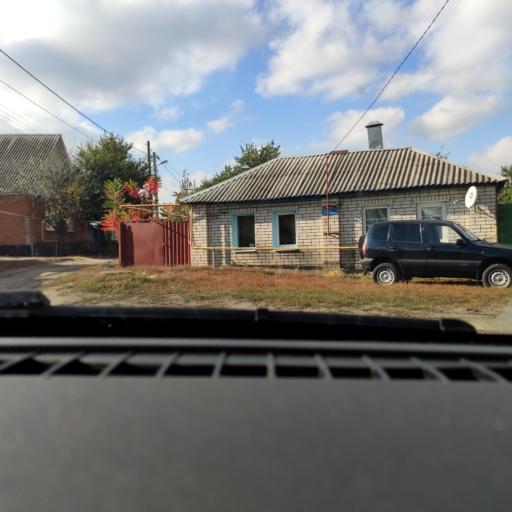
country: RU
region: Voronezj
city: Voronezh
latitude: 51.6779
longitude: 39.2457
